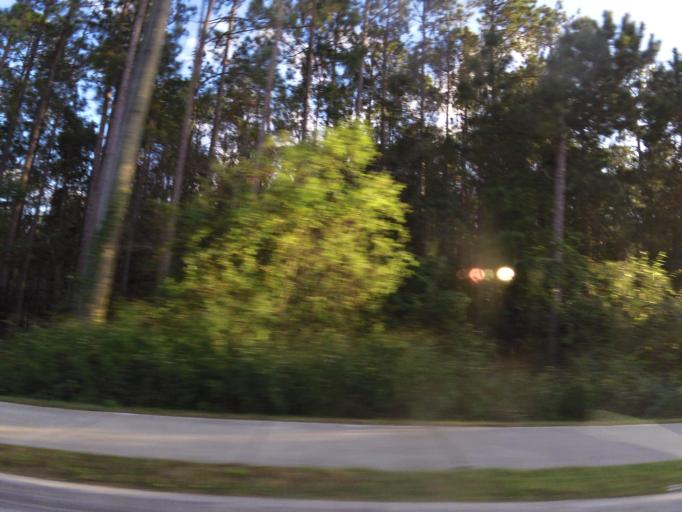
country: US
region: Florida
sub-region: Saint Johns County
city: Fruit Cove
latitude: 30.0599
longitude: -81.5124
